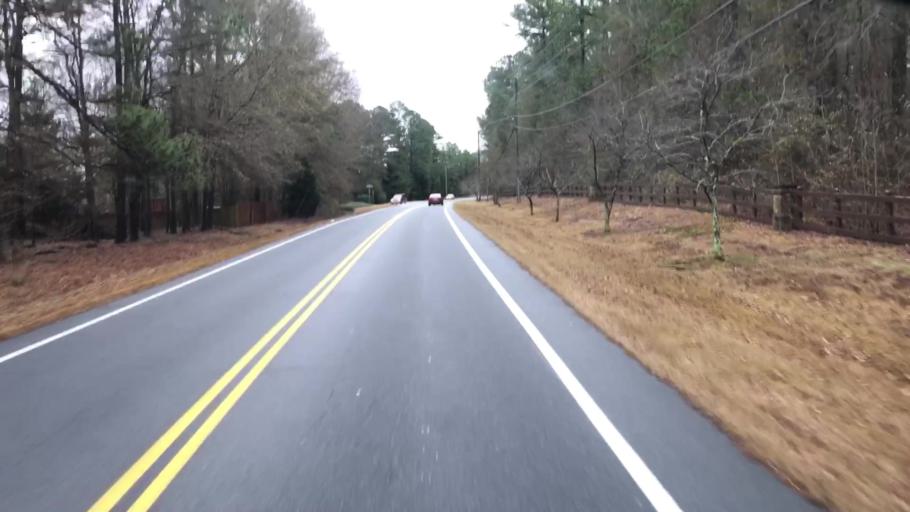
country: US
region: Georgia
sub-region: Gwinnett County
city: Snellville
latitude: 33.8251
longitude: -83.9808
